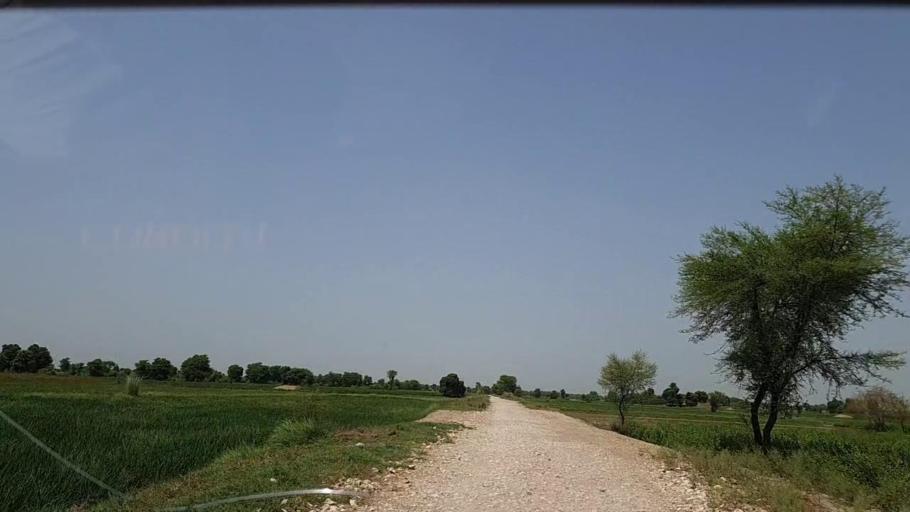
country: PK
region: Sindh
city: Tharu Shah
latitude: 26.9497
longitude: 68.0437
